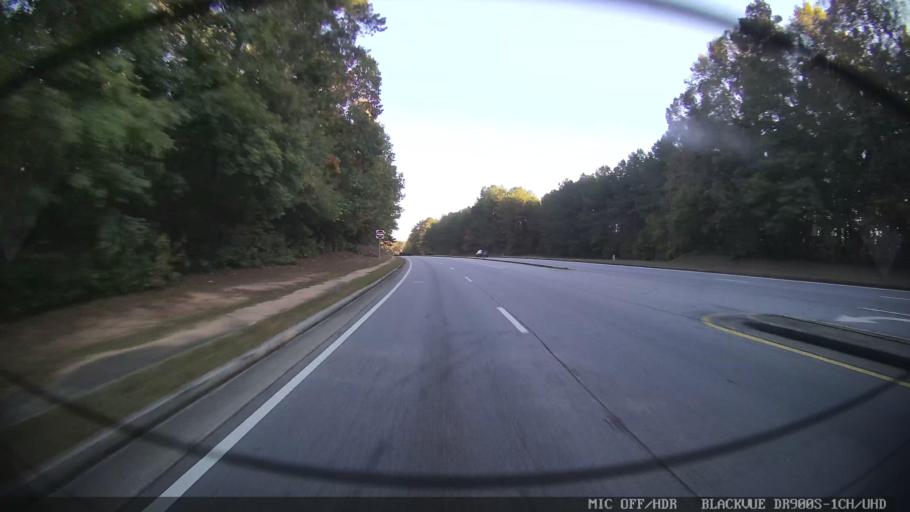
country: US
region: Georgia
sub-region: Clayton County
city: Jonesboro
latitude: 33.5340
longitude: -84.3402
